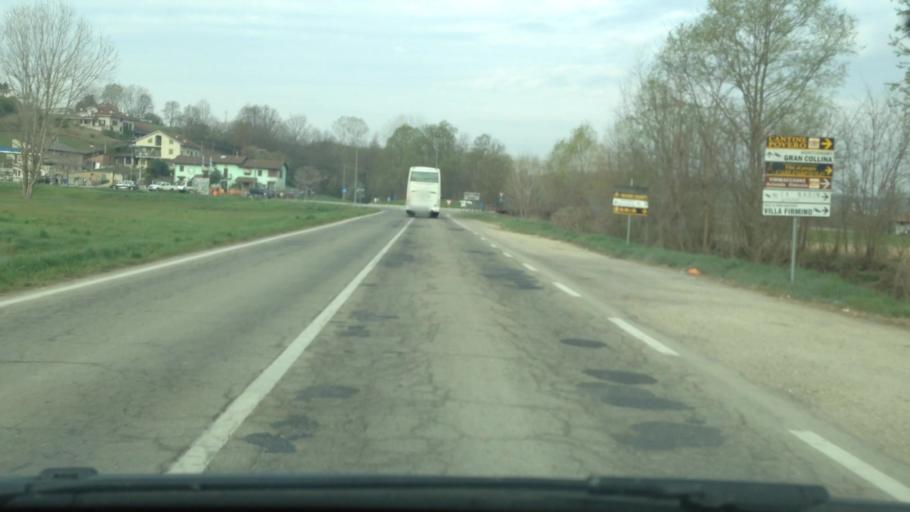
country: IT
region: Piedmont
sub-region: Provincia di Asti
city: San Damiano d'Asti
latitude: 44.8453
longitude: 8.0731
